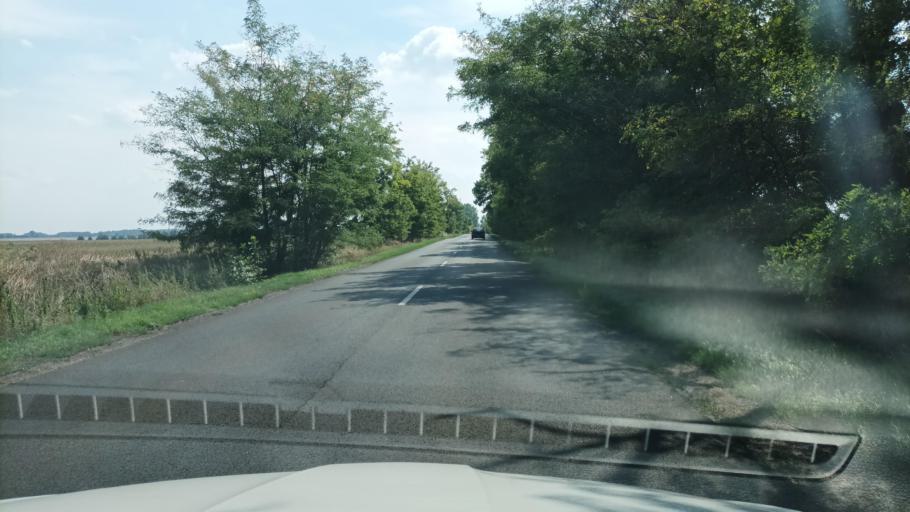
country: HU
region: Pest
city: Zsambok
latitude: 47.5653
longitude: 19.6030
